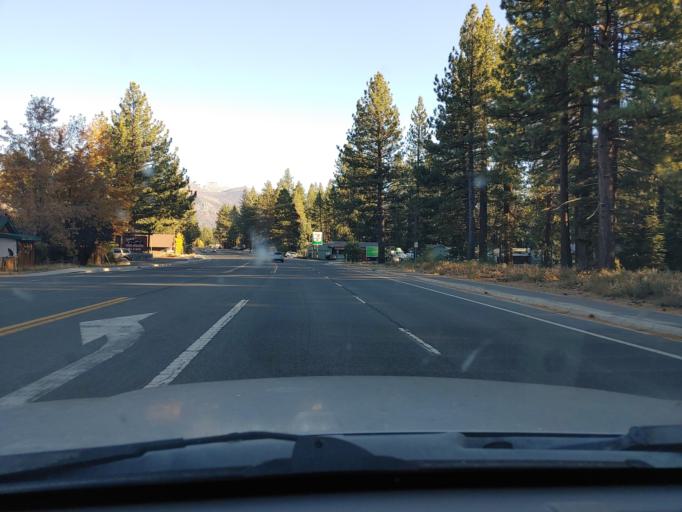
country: US
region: California
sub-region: El Dorado County
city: South Lake Tahoe
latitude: 38.9187
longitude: -120.0123
